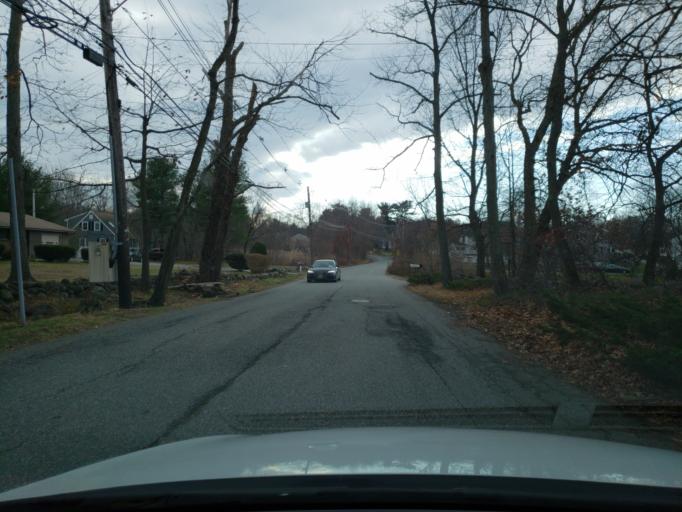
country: US
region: Massachusetts
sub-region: Essex County
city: Andover
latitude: 42.6624
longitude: -71.1178
